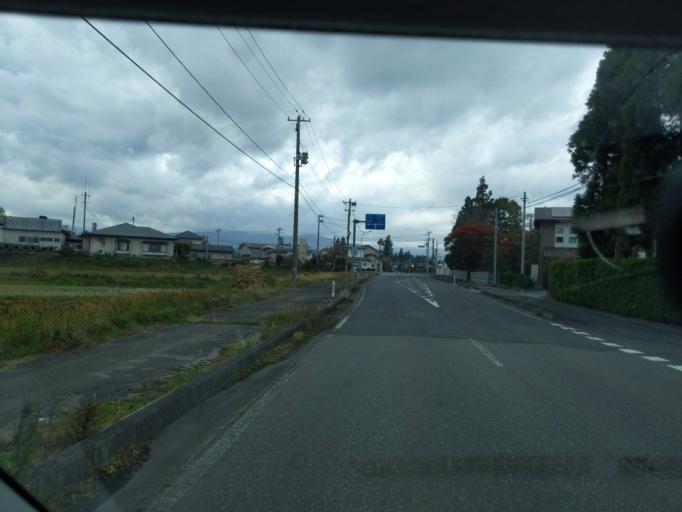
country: JP
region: Iwate
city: Mizusawa
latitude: 39.1304
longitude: 141.0659
